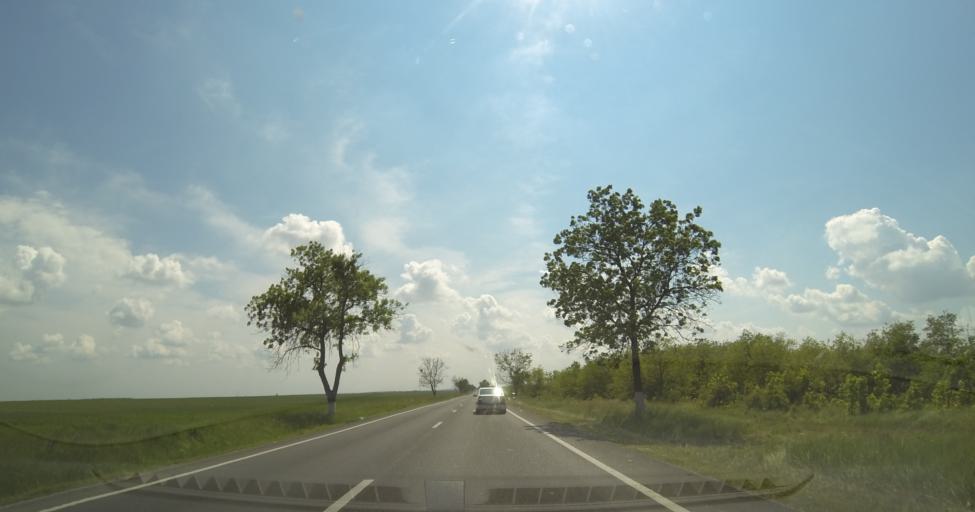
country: RO
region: Arges
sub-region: Comuna Sapata
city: Martesti
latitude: 44.7137
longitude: 24.7921
